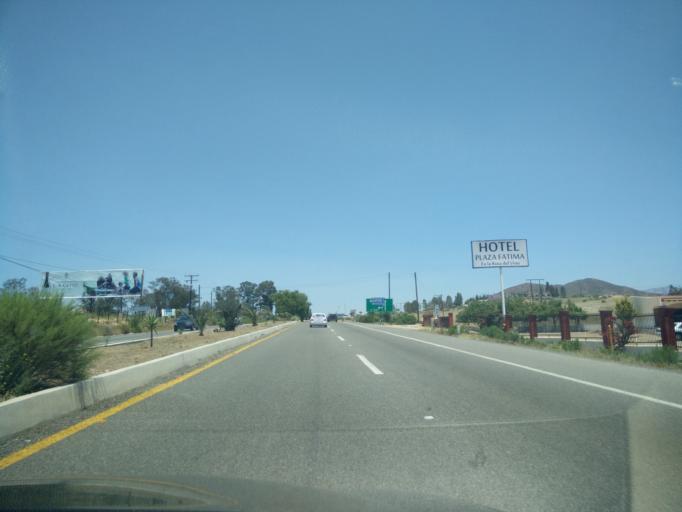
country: MX
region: Baja California
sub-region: Ensenada
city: Rancho Verde
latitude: 31.9907
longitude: -116.6425
